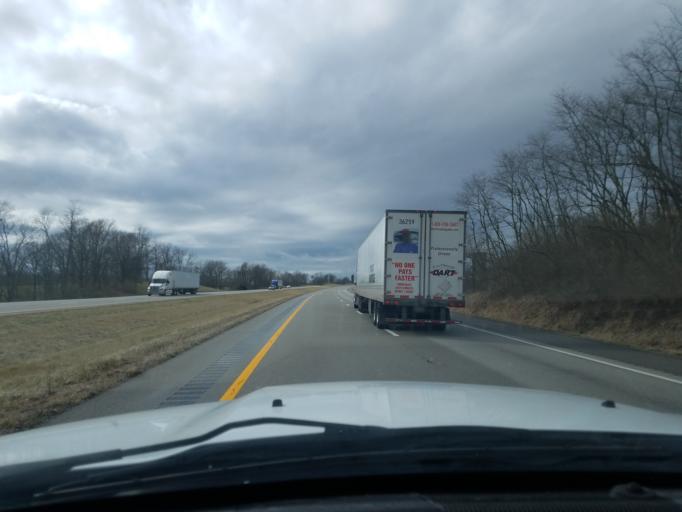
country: US
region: Kentucky
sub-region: Montgomery County
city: Mount Sterling
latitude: 38.0910
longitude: -83.8816
